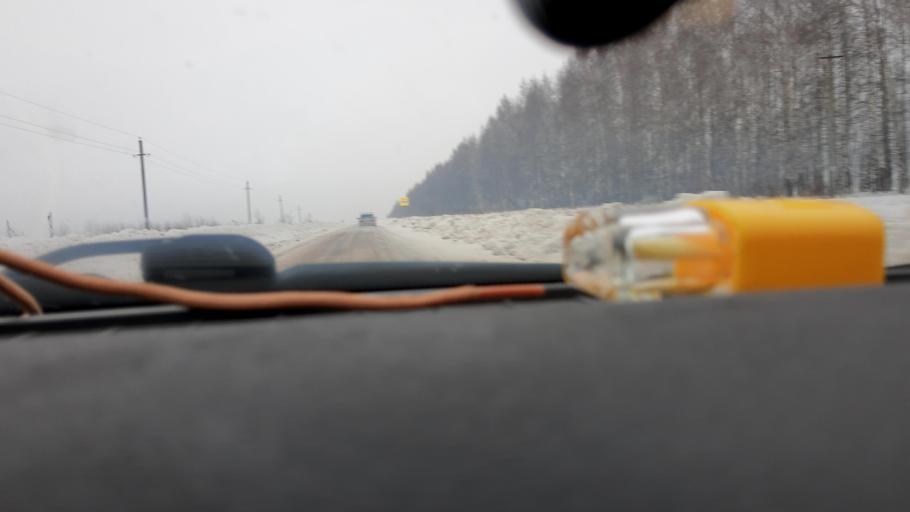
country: RU
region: Bashkortostan
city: Ulukulevo
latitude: 54.5689
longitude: 56.4306
